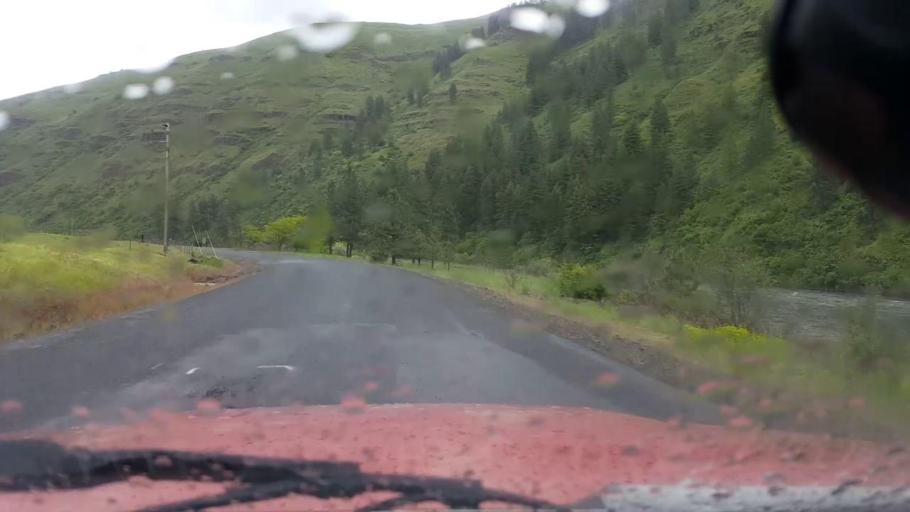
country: US
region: Washington
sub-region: Asotin County
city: Asotin
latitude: 46.0354
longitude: -117.2755
